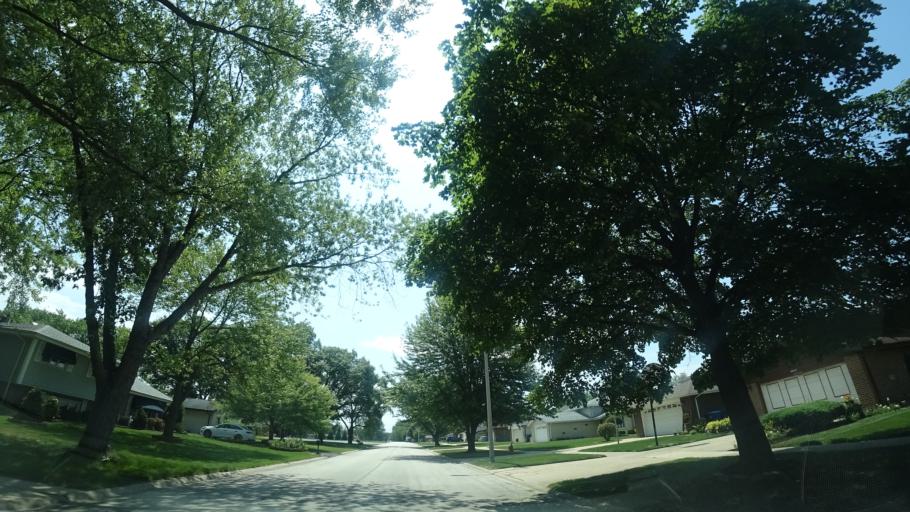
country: US
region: Illinois
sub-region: Cook County
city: Crestwood
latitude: 41.6633
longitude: -87.7631
